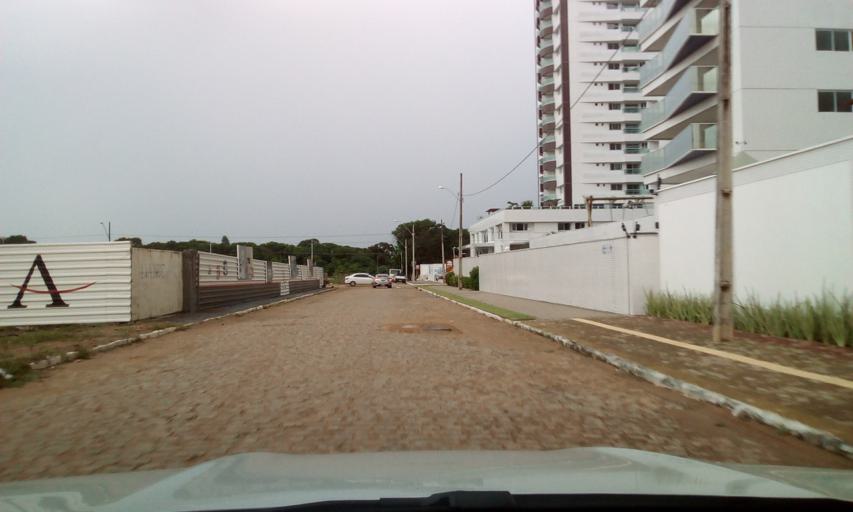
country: BR
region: Paraiba
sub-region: Joao Pessoa
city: Joao Pessoa
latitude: -7.1330
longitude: -34.8266
